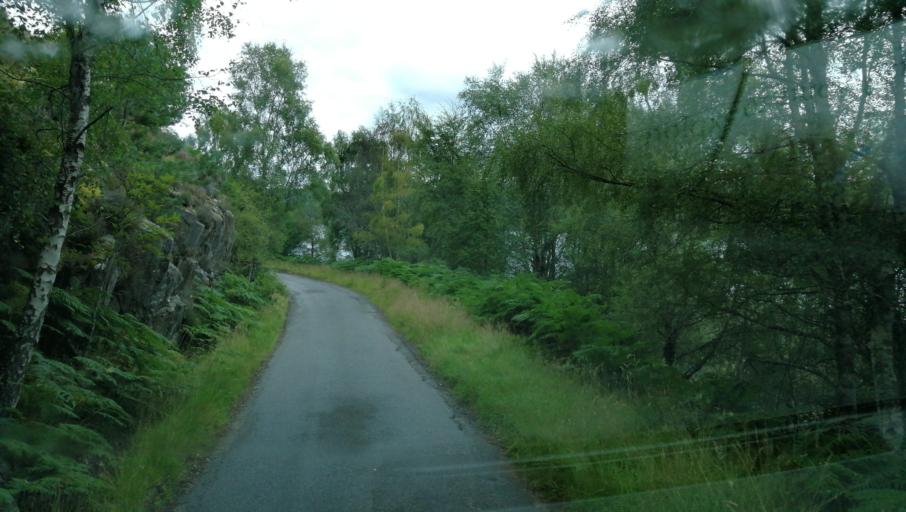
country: GB
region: Scotland
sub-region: Highland
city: Spean Bridge
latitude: 57.2738
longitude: -4.9598
